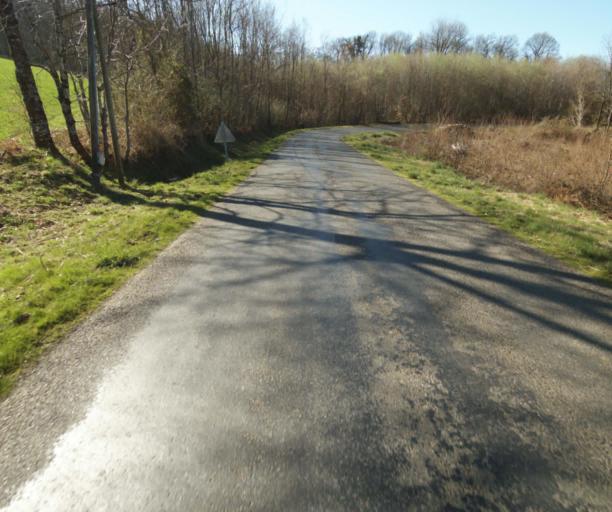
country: FR
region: Limousin
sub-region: Departement de la Correze
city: Seilhac
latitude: 45.3976
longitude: 1.7477
